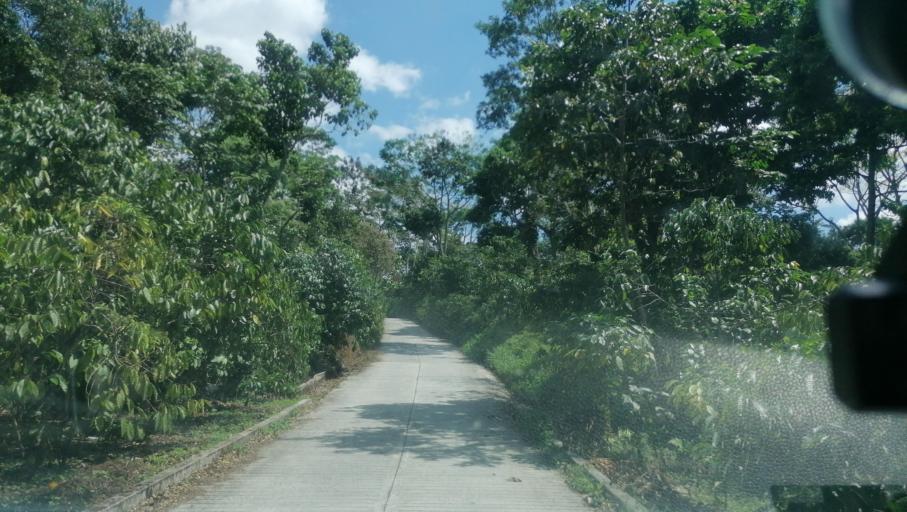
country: MX
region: Chiapas
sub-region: Union Juarez
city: Santo Domingo
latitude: 15.0425
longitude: -92.1475
